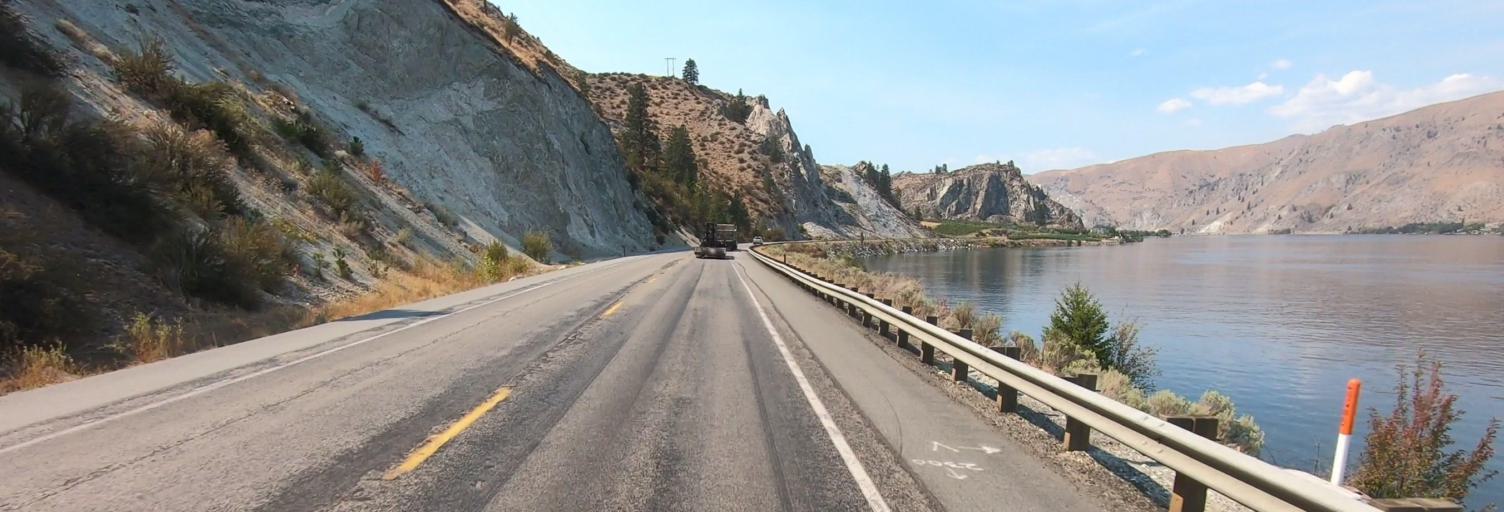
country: US
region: Washington
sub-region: Chelan County
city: Chelan
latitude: 47.7610
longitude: -120.0900
